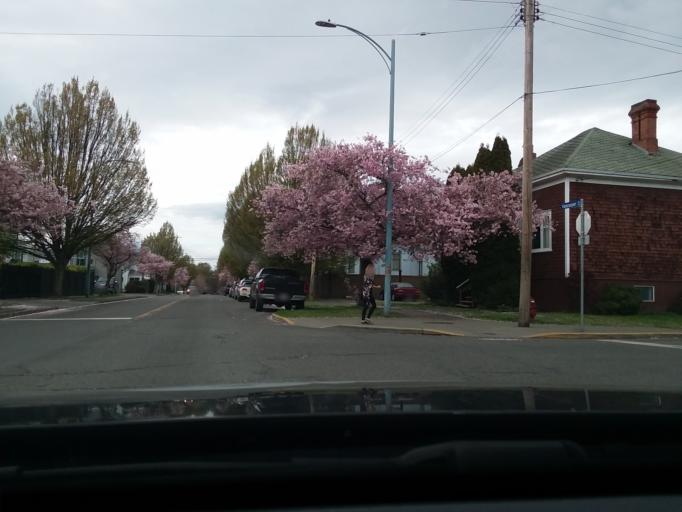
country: CA
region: British Columbia
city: Victoria
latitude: 48.4288
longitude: -123.3560
